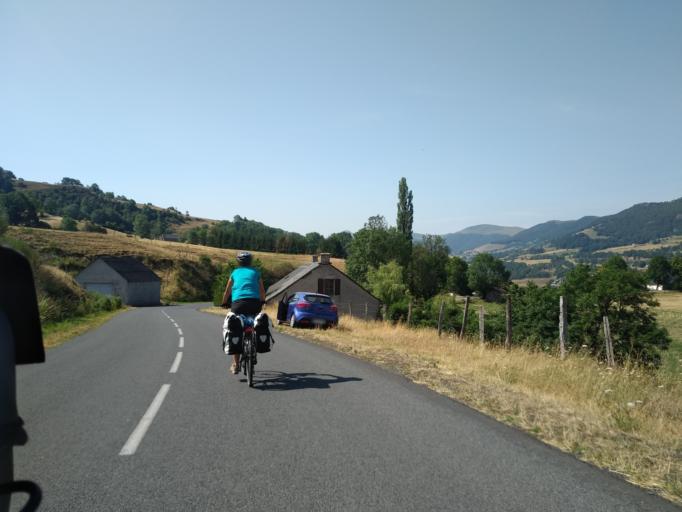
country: FR
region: Auvergne
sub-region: Departement du Cantal
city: Riom-es-Montagnes
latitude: 45.2136
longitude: 2.7193
